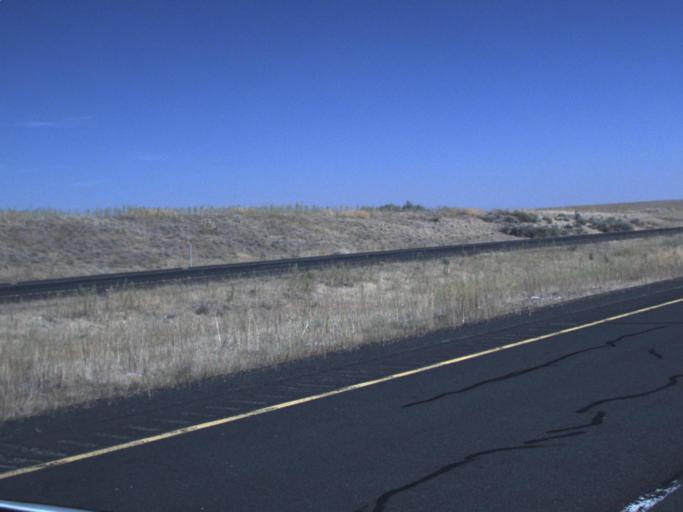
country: US
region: Washington
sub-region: Adams County
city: Ritzville
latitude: 47.1112
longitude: -118.4509
